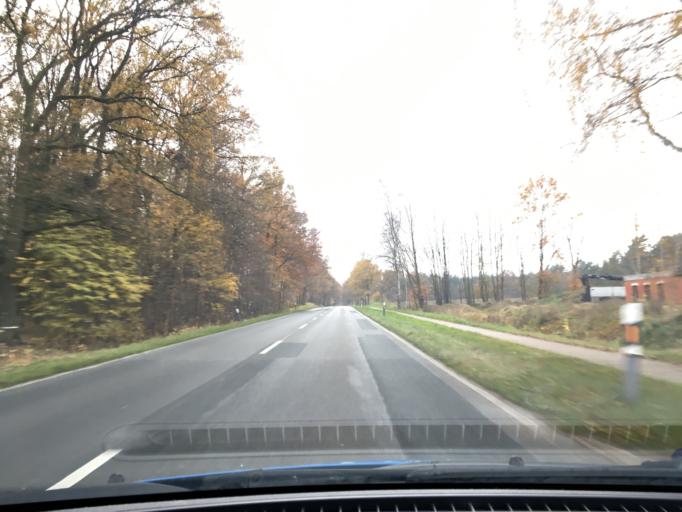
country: DE
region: Lower Saxony
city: Embsen
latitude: 53.2048
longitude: 10.3608
